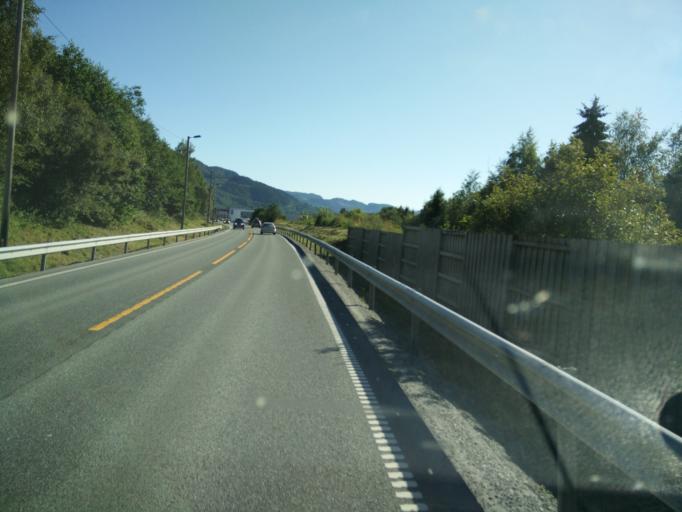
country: NO
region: Sor-Trondelag
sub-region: Orkdal
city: Orkanger
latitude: 63.3033
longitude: 9.8524
